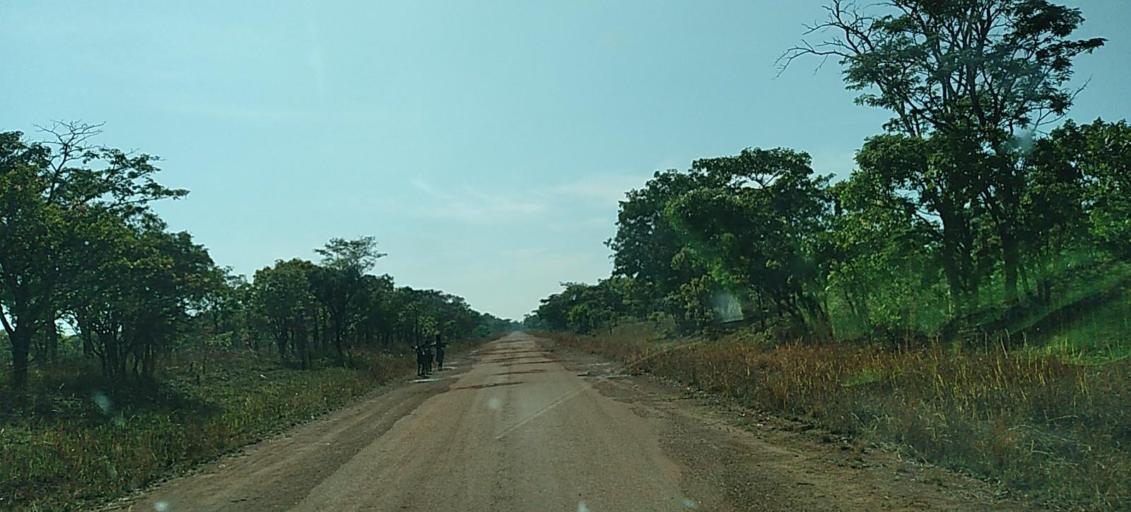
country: ZM
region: North-Western
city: Mwinilunga
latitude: -11.7899
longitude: 25.0613
